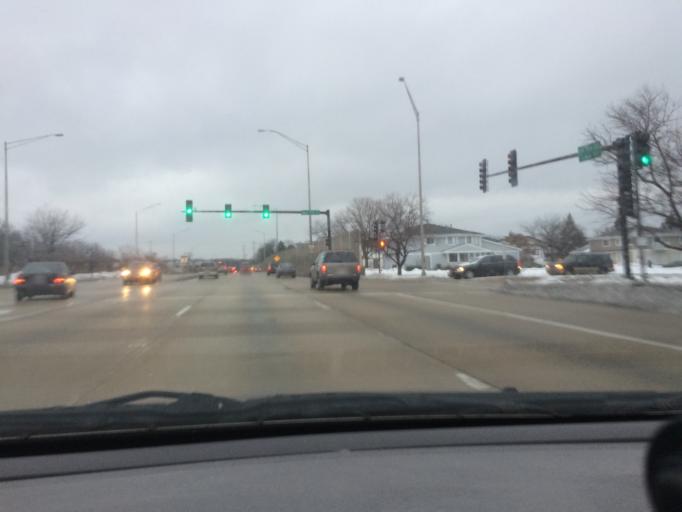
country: US
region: Illinois
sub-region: DuPage County
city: Hanover Park
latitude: 41.9848
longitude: -88.1430
